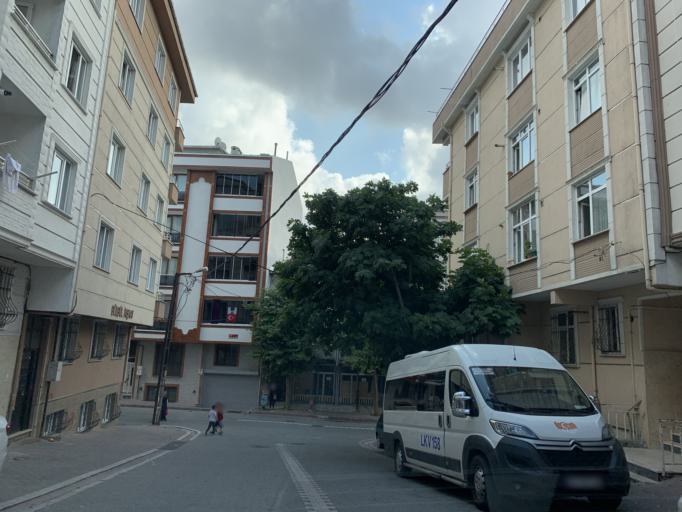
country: TR
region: Istanbul
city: Esenyurt
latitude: 41.0237
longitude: 28.6737
